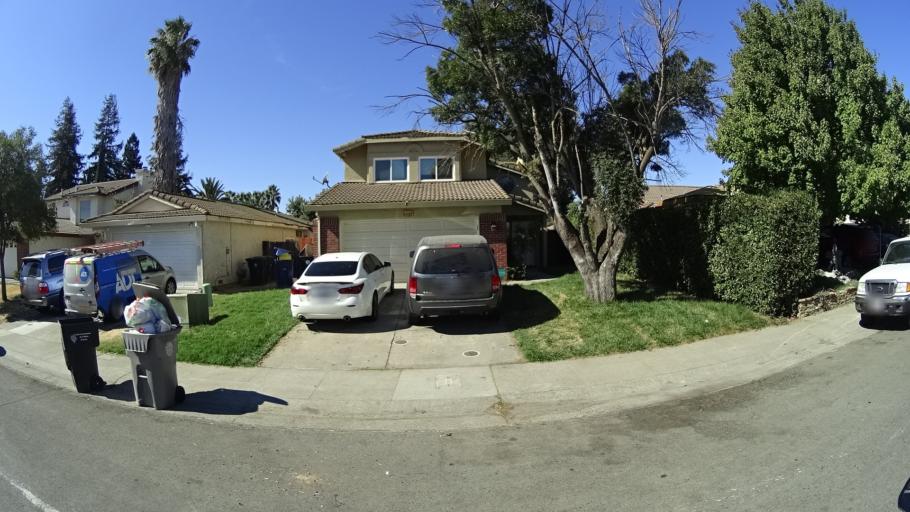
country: US
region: California
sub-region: Sacramento County
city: Parkway
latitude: 38.4648
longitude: -121.4449
